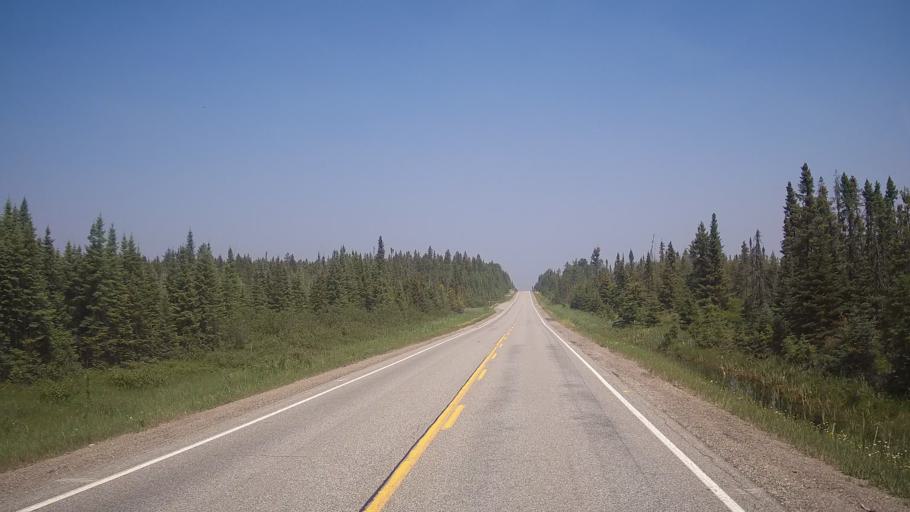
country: CA
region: Ontario
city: Timmins
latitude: 48.1766
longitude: -81.5823
